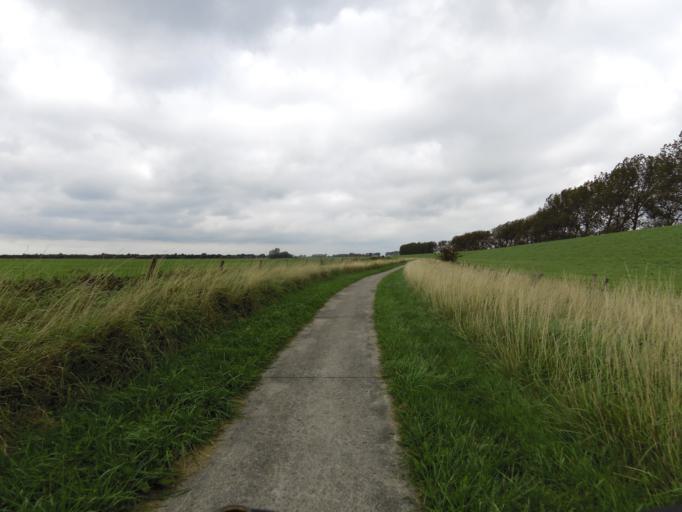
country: NL
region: South Holland
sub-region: Gemeente Goeree-Overflakkee
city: Dirksland
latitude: 51.7572
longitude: 4.0487
